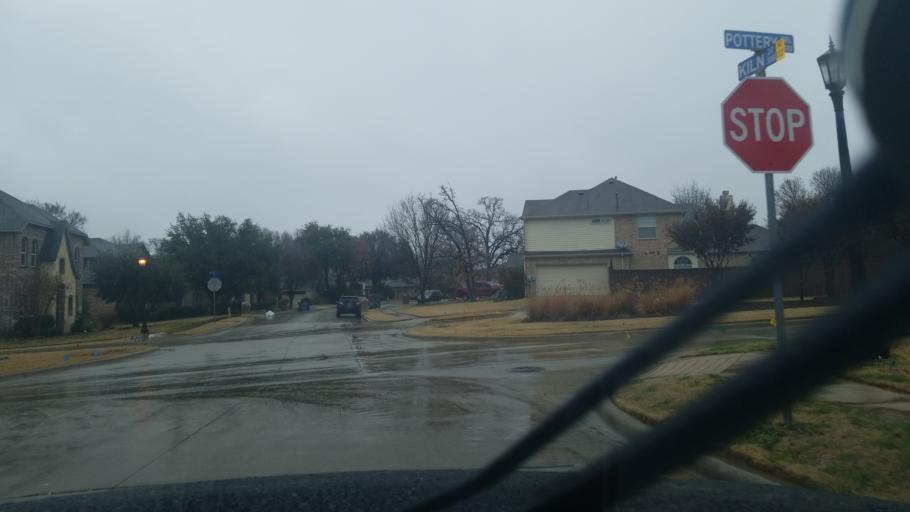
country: US
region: Texas
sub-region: Denton County
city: Corinth
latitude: 33.1342
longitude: -97.0935
